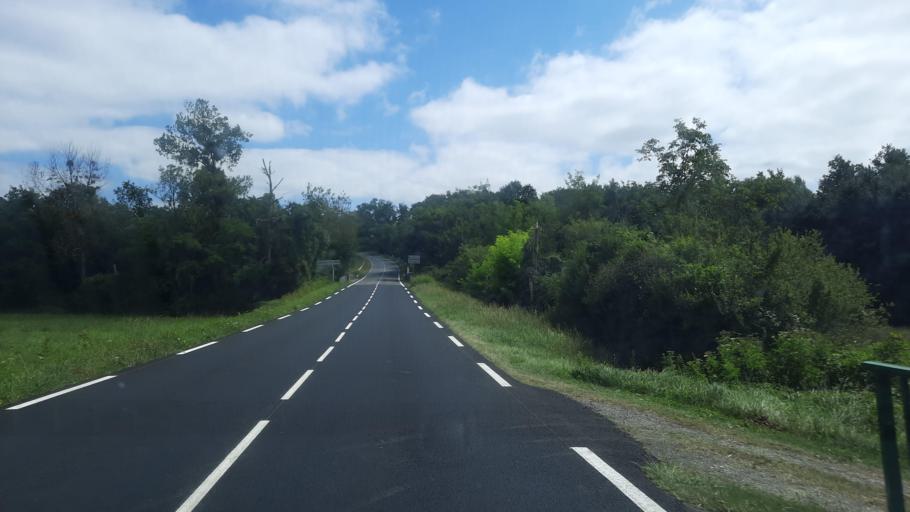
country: FR
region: Midi-Pyrenees
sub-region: Departement de la Haute-Garonne
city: Boulogne-sur-Gesse
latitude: 43.2928
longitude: 0.6299
